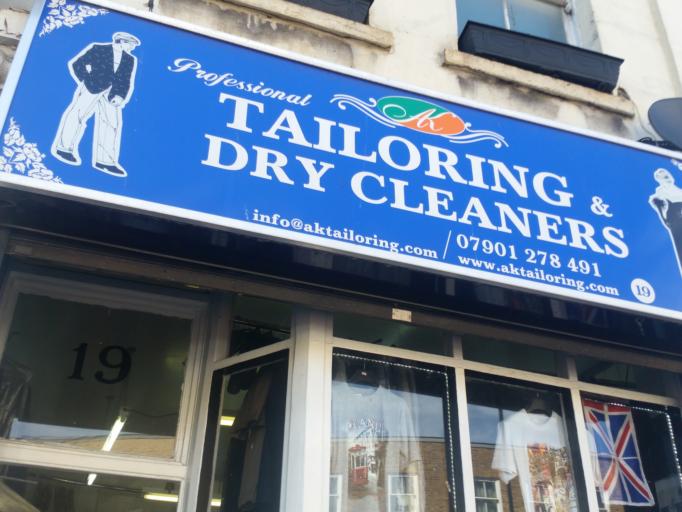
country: GB
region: England
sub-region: Greater London
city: Bethnal Green
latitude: 51.5349
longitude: -0.0574
